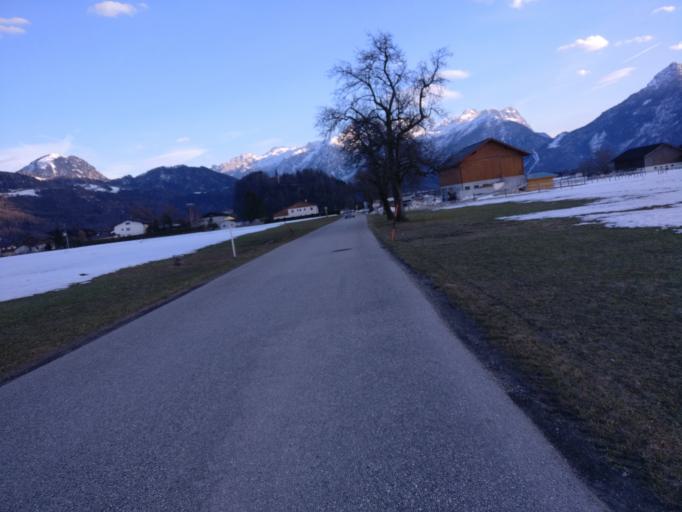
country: AT
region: Salzburg
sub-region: Politischer Bezirk Hallein
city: Kuchl
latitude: 47.6423
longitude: 13.1514
